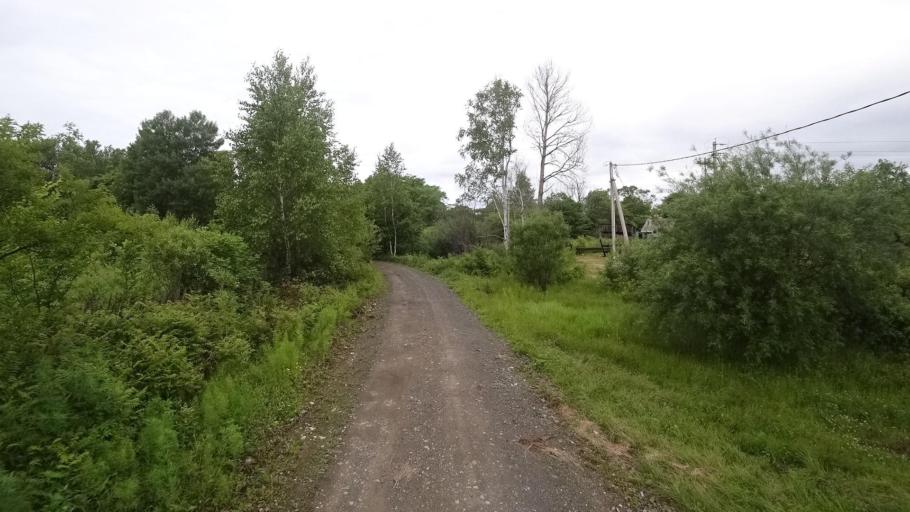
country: RU
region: Khabarovsk Krai
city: Amursk
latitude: 49.9043
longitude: 136.1355
